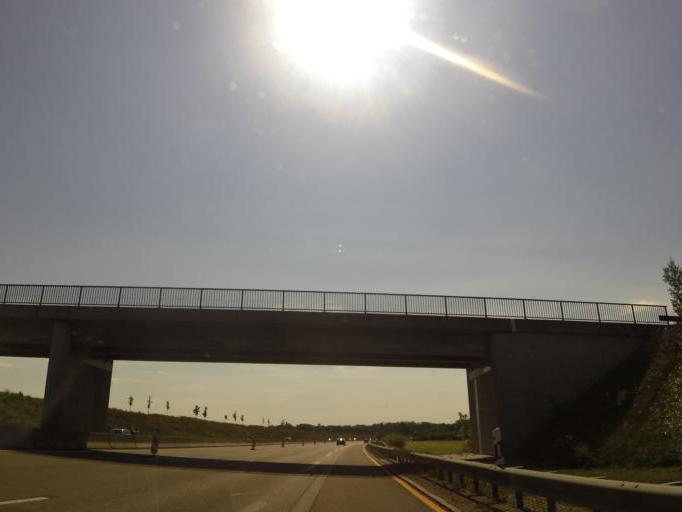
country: DE
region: Bavaria
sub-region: Swabia
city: Leipheim
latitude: 48.4568
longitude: 10.1909
